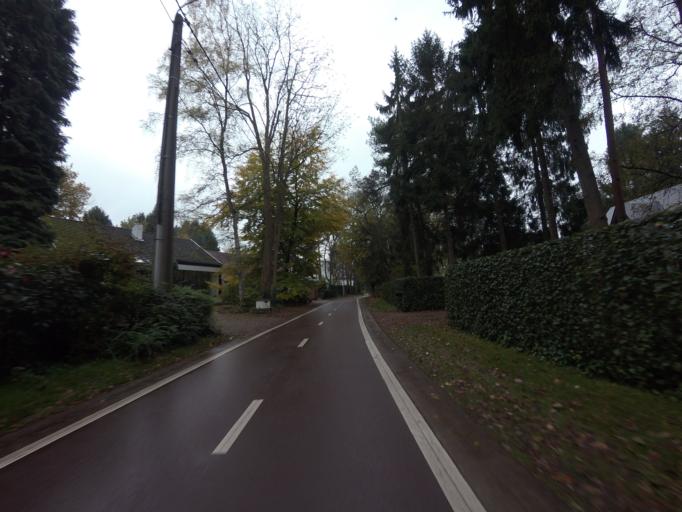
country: BE
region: Flanders
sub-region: Provincie Antwerpen
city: Bonheiden
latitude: 51.0256
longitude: 4.5307
